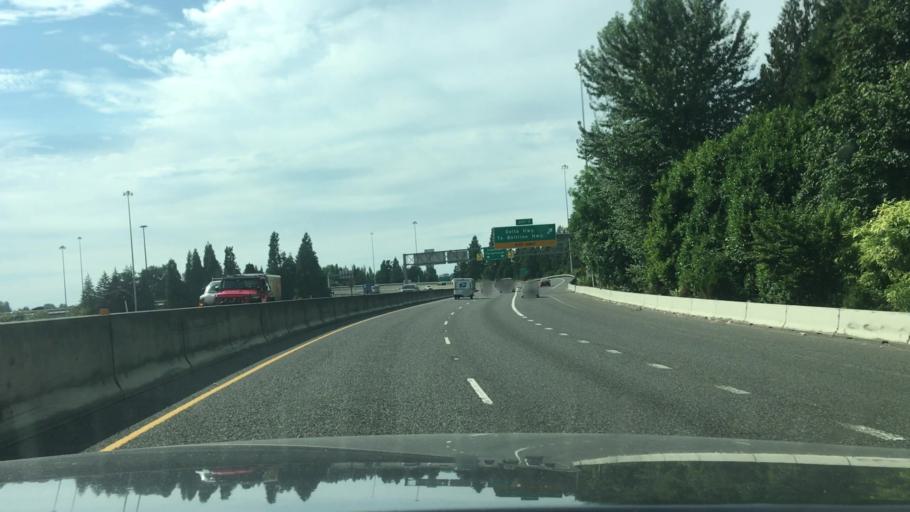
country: US
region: Oregon
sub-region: Lane County
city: Eugene
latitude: 44.0634
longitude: -123.0951
